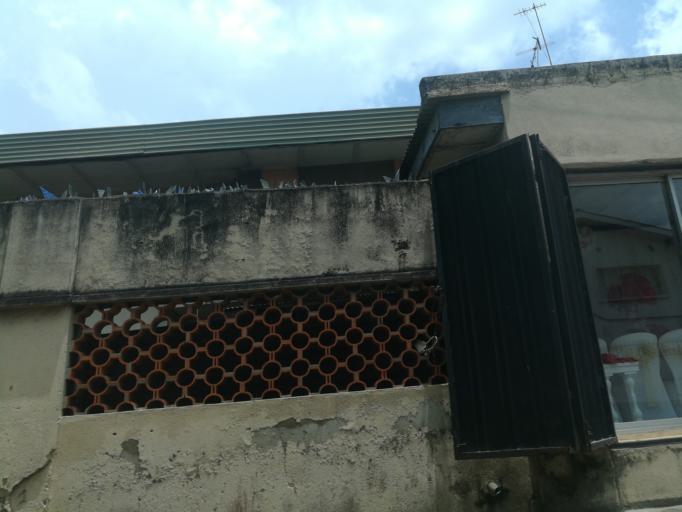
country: NG
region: Lagos
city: Somolu
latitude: 6.5520
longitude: 3.3606
